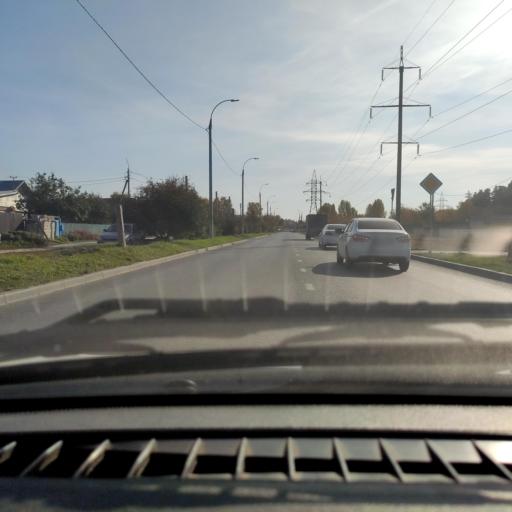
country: RU
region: Samara
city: Tol'yatti
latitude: 53.5167
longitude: 49.3953
